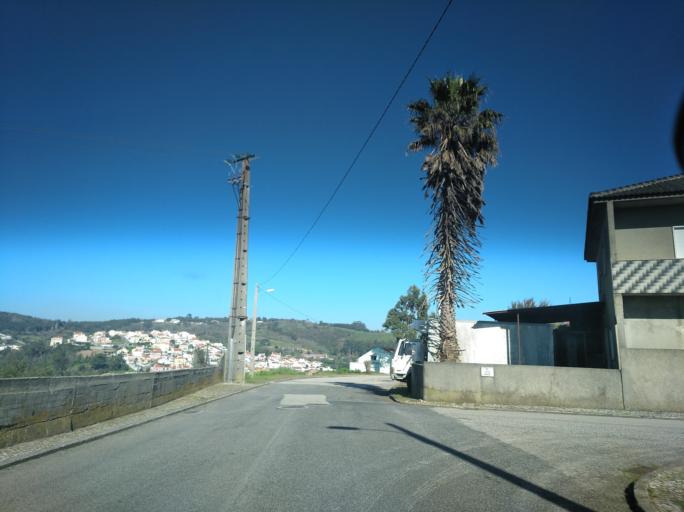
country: PT
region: Lisbon
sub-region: Odivelas
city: Canecas
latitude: 38.8114
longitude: -9.2169
